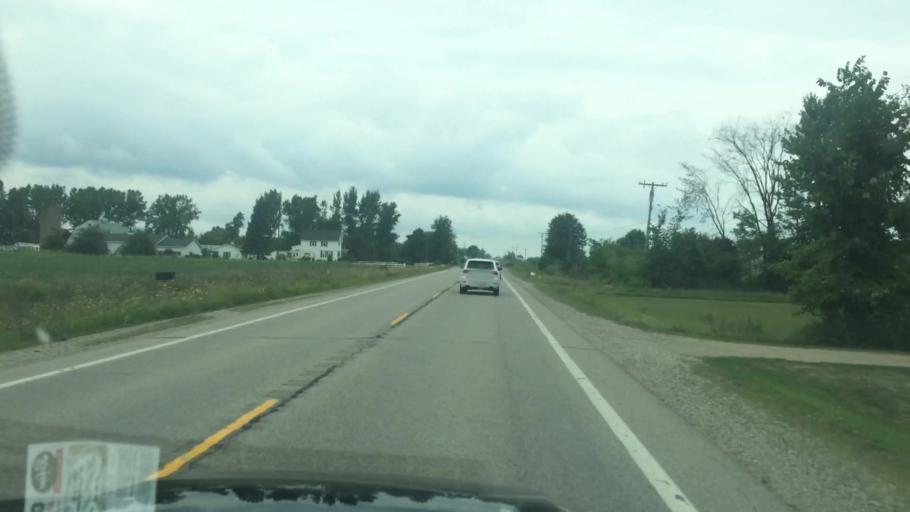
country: US
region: Michigan
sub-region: Tuscola County
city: Cass City
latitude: 43.5100
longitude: -83.0923
